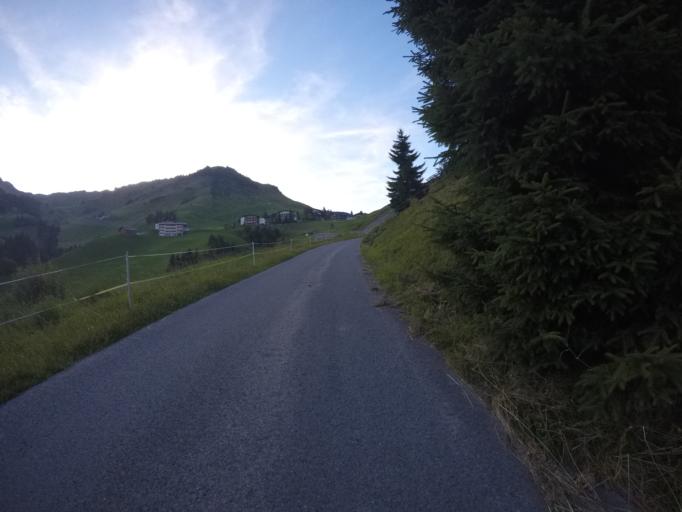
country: AT
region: Vorarlberg
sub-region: Politischer Bezirk Bregenz
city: Damuels
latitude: 47.2662
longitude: 9.9097
